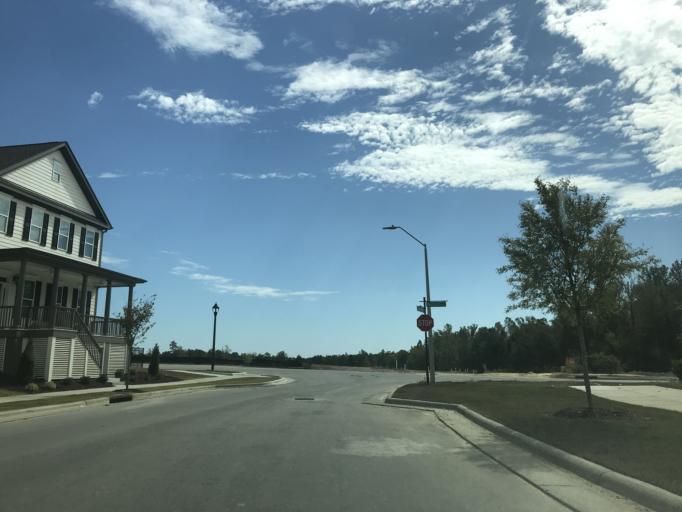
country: US
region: North Carolina
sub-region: Wake County
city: Knightdale
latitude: 35.8599
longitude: -78.5396
